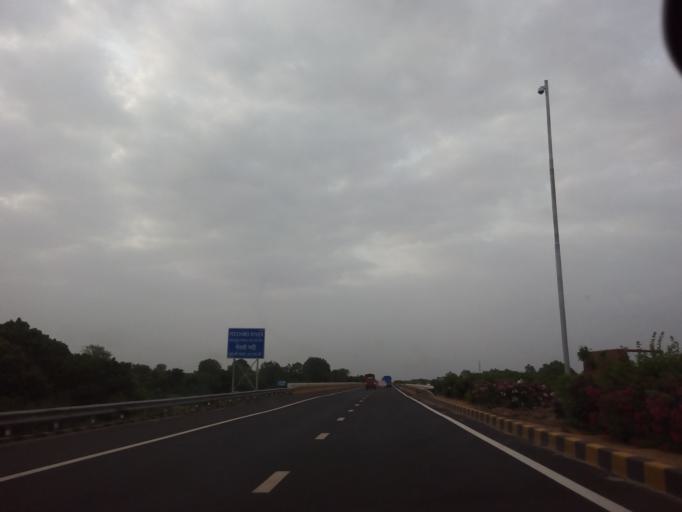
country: IN
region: Gujarat
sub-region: Kheda
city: Mahemdavad
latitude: 22.9147
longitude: 72.7613
